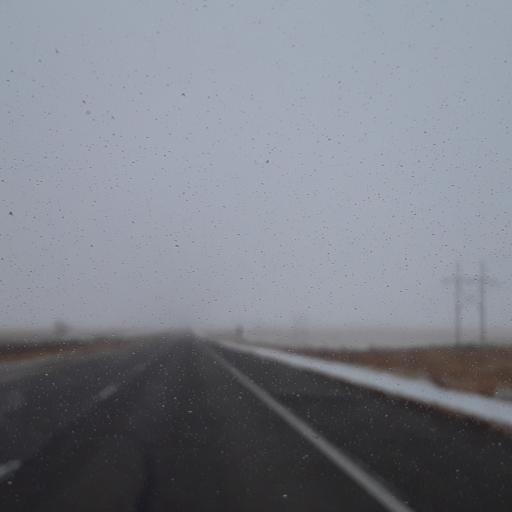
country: US
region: Colorado
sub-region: Logan County
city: Sterling
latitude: 40.7913
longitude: -102.8890
